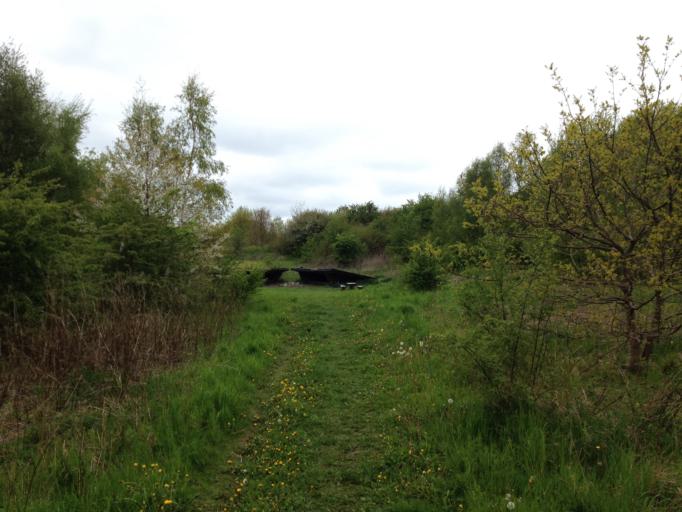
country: DK
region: Capital Region
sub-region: Fredensborg Kommune
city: Niva
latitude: 55.9482
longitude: 12.5041
